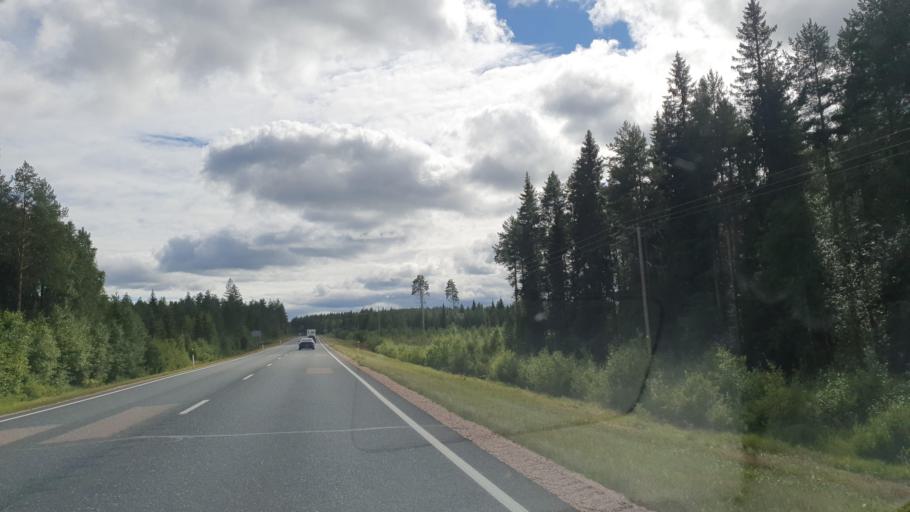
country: FI
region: Kainuu
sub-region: Kajaani
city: Kajaani
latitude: 64.1026
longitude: 27.4489
